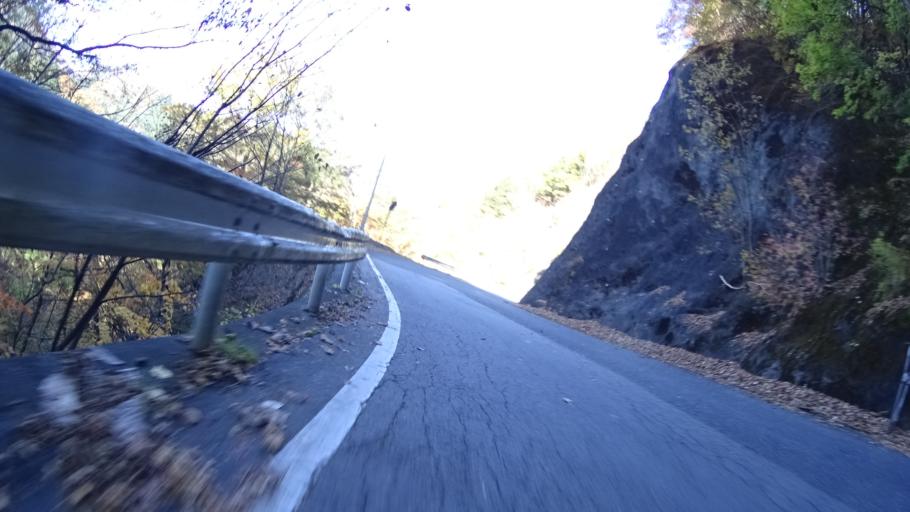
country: JP
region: Yamanashi
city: Otsuki
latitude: 35.7754
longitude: 138.9238
